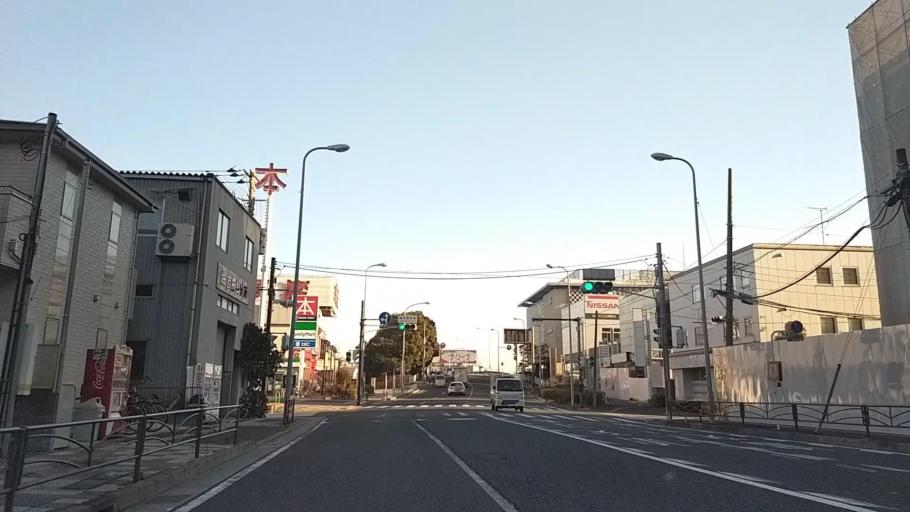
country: JP
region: Kanagawa
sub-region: Kawasaki-shi
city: Kawasaki
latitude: 35.5111
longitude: 139.6839
